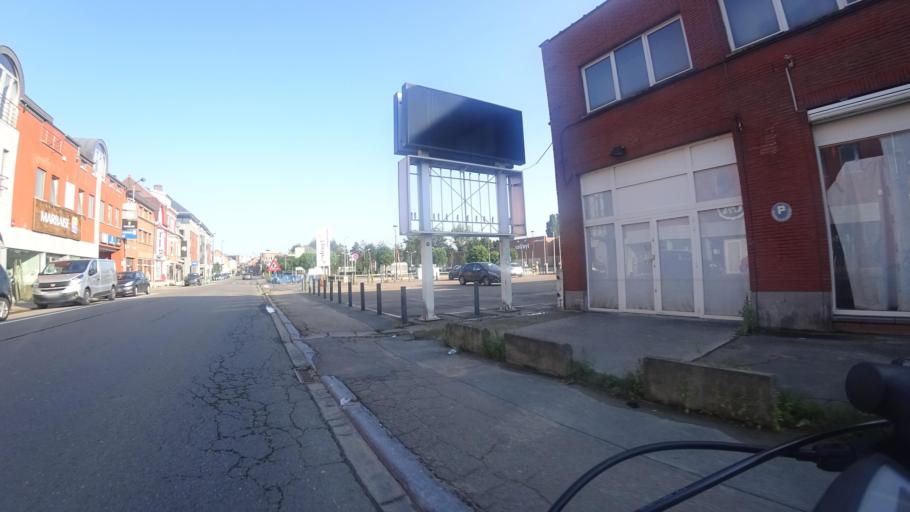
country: BE
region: Wallonia
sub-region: Province du Brabant Wallon
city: Wavre
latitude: 50.7164
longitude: 4.6164
